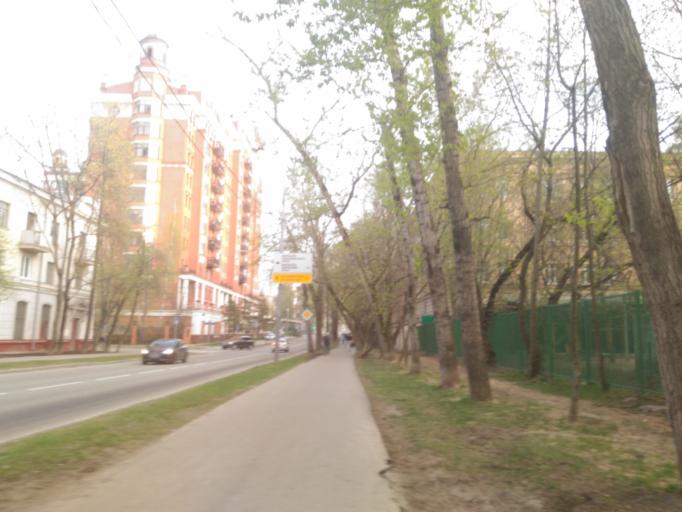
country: RU
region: Moskovskaya
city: Khoroshevo-Mnevniki
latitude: 55.7937
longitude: 37.4832
